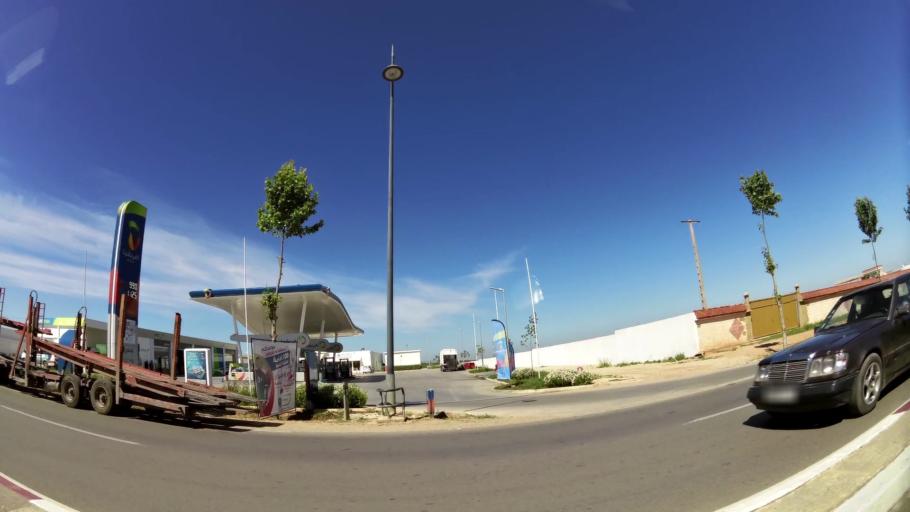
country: MA
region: Meknes-Tafilalet
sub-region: Meknes
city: Meknes
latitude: 33.8408
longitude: -5.5213
